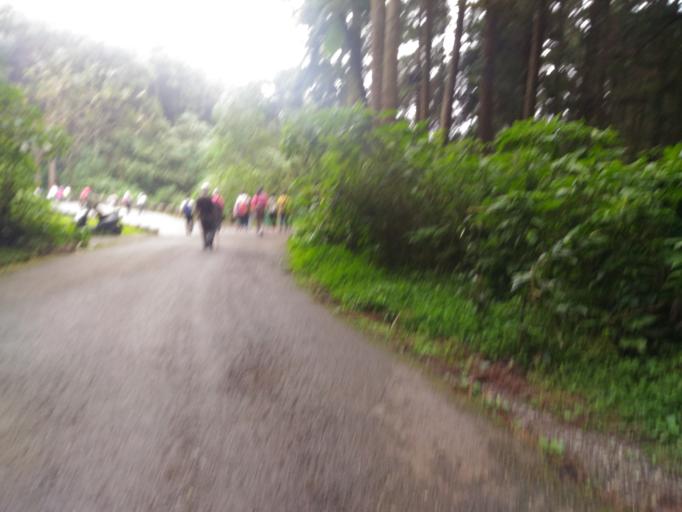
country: TW
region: Taiwan
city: Lugu
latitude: 23.6661
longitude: 120.7929
